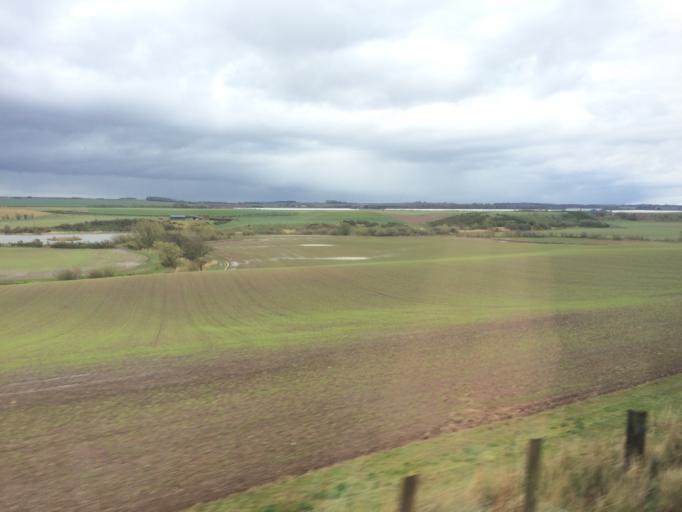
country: GB
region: Scotland
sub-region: Angus
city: Montrose
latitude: 56.6516
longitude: -2.5261
